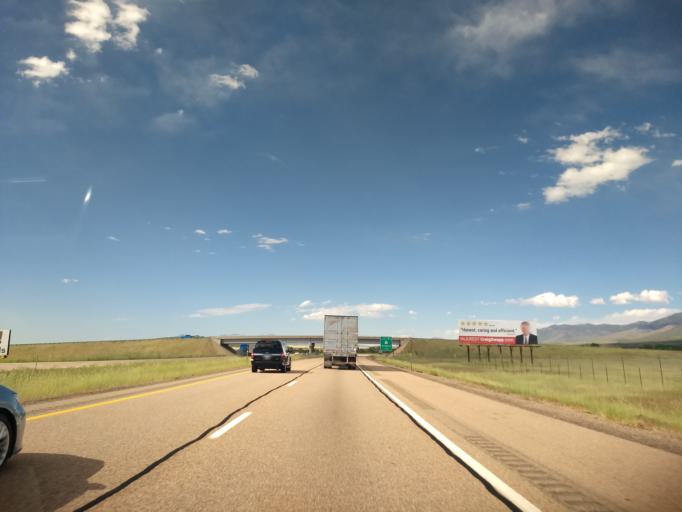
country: US
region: Utah
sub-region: Millard County
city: Fillmore
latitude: 38.9765
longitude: -112.3394
